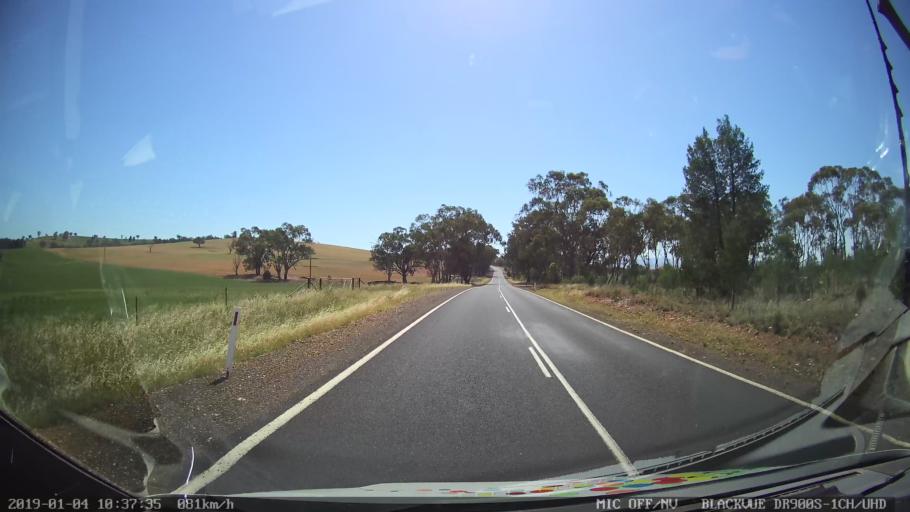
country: AU
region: New South Wales
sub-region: Cabonne
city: Molong
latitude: -33.2954
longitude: 148.6967
